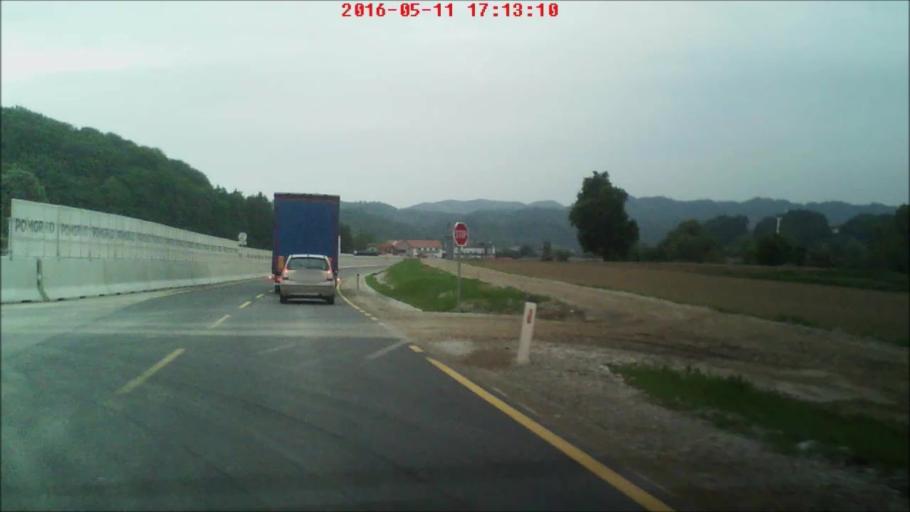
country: SI
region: Podlehnik
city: Podlehnik
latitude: 46.3425
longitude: 15.8737
